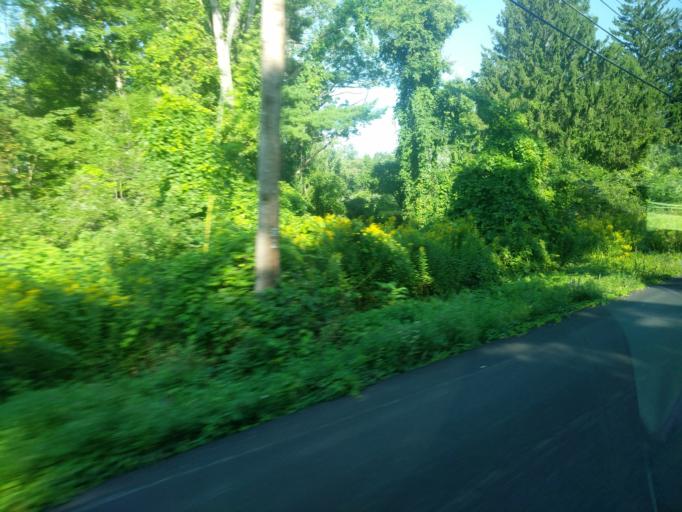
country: US
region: Massachusetts
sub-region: Berkshire County
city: Great Barrington
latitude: 42.2100
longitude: -73.3639
